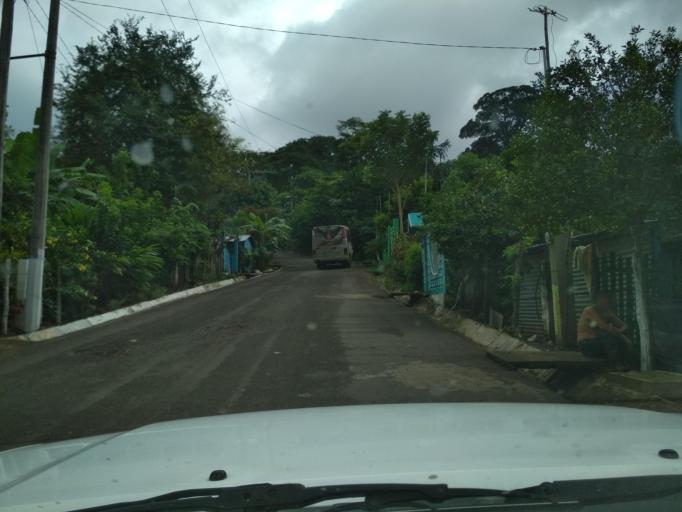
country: MX
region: Veracruz
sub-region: San Andres Tuxtla
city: El Huidero
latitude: 18.3852
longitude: -95.1786
